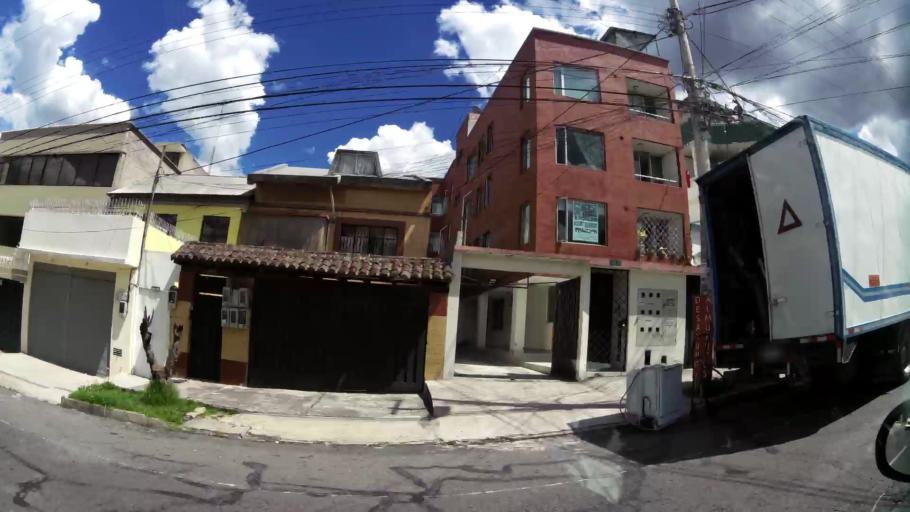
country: EC
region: Pichincha
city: Quito
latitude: -0.1919
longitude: -78.4997
